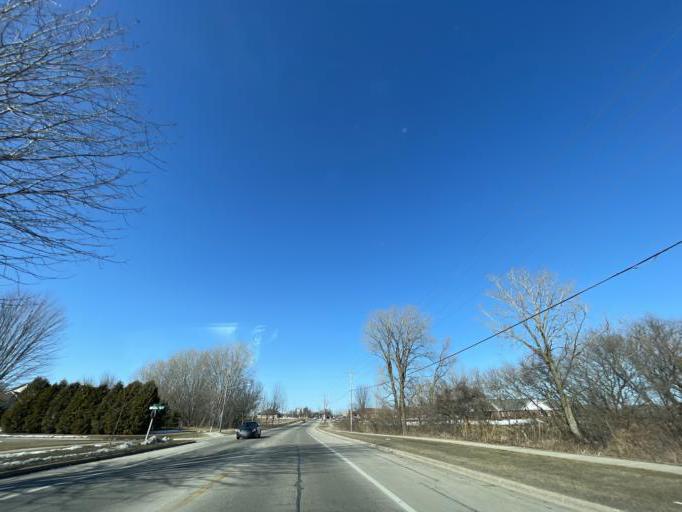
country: US
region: Wisconsin
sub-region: Brown County
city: Howard
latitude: 44.5874
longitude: -88.0843
